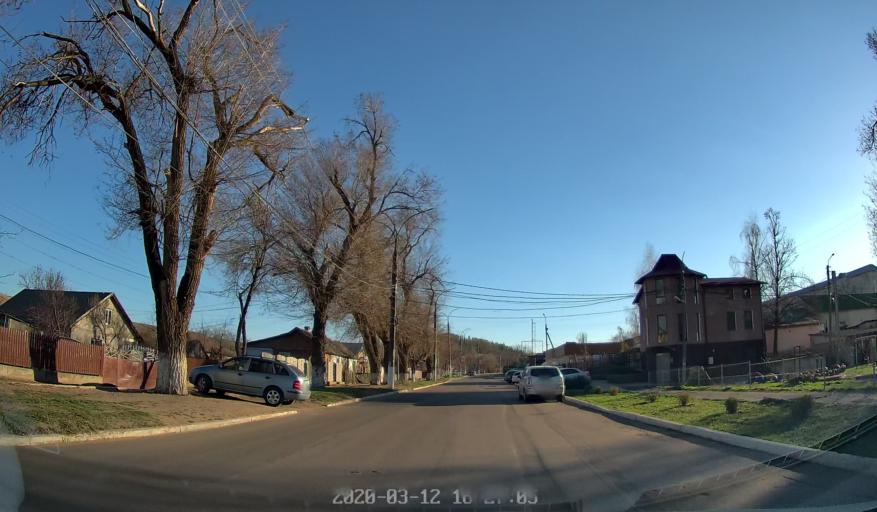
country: MD
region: Anenii Noi
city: Anenii Noi
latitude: 46.8777
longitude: 29.2316
